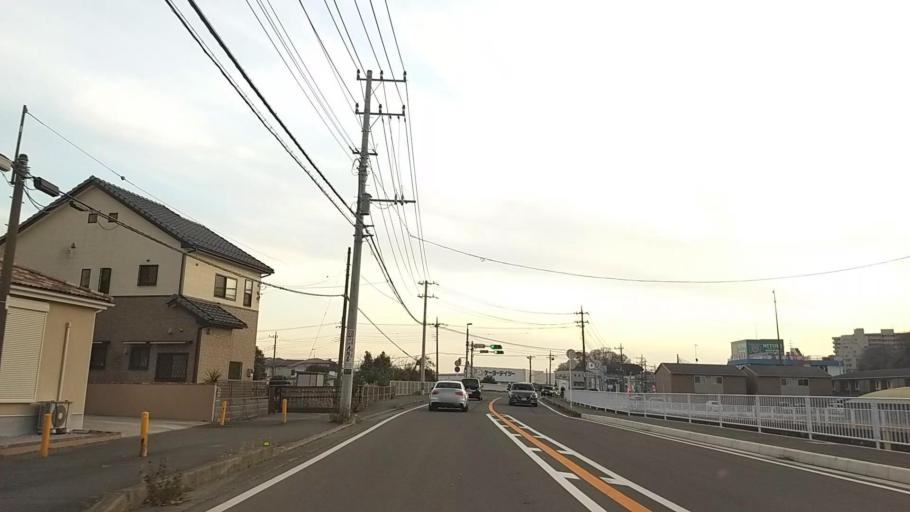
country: JP
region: Kanagawa
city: Atsugi
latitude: 35.4324
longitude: 139.3527
